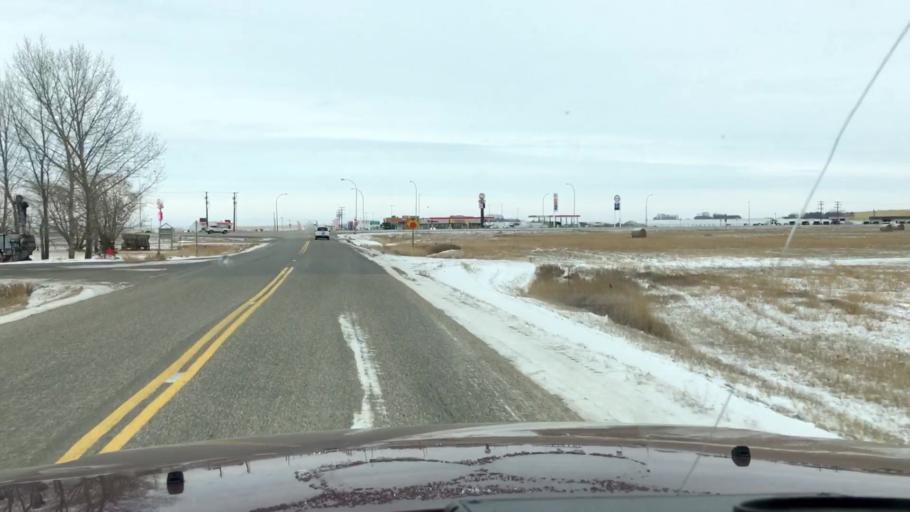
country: CA
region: Saskatchewan
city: Watrous
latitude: 51.2489
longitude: -105.9728
